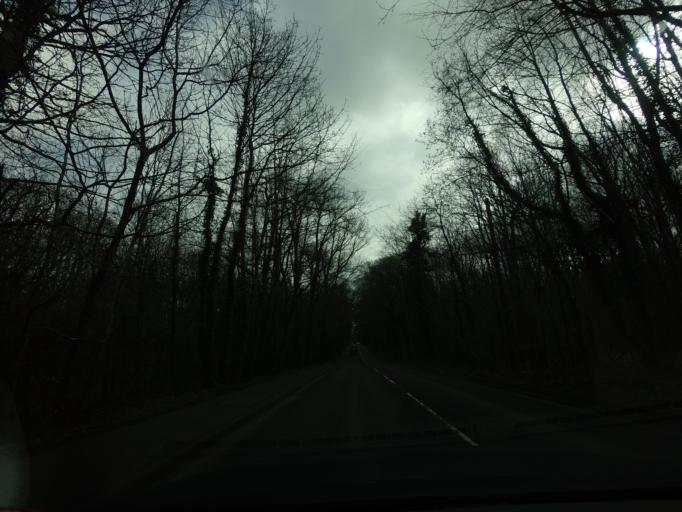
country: GB
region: England
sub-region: Kent
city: Kemsing
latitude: 51.2847
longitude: 0.2383
